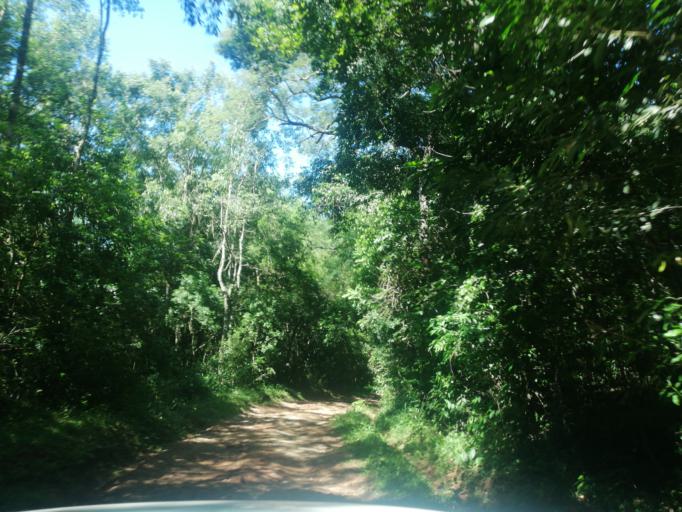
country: AR
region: Misiones
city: Cerro Azul
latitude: -27.7419
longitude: -55.5704
